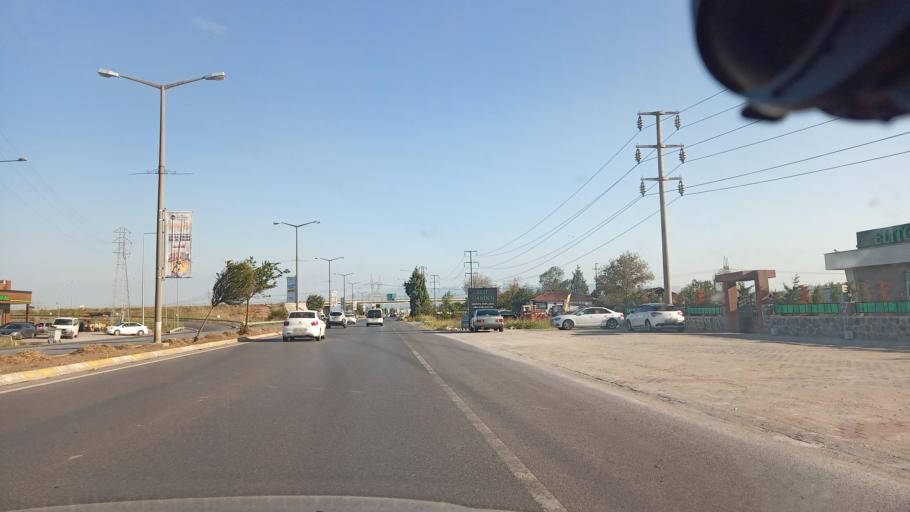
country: TR
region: Sakarya
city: Kazimpasa
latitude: 40.8307
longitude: 30.3486
